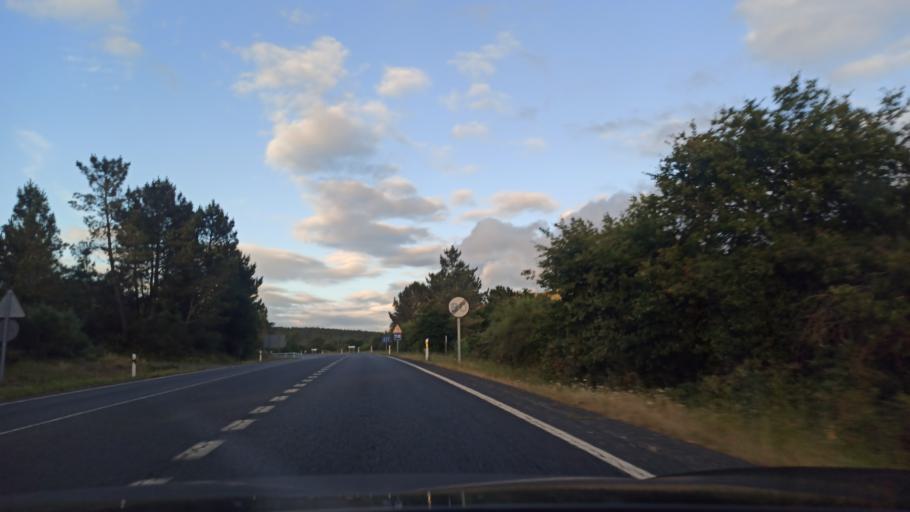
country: ES
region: Galicia
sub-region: Provincia de Pontevedra
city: Rodeiro
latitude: 42.7683
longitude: -7.9778
